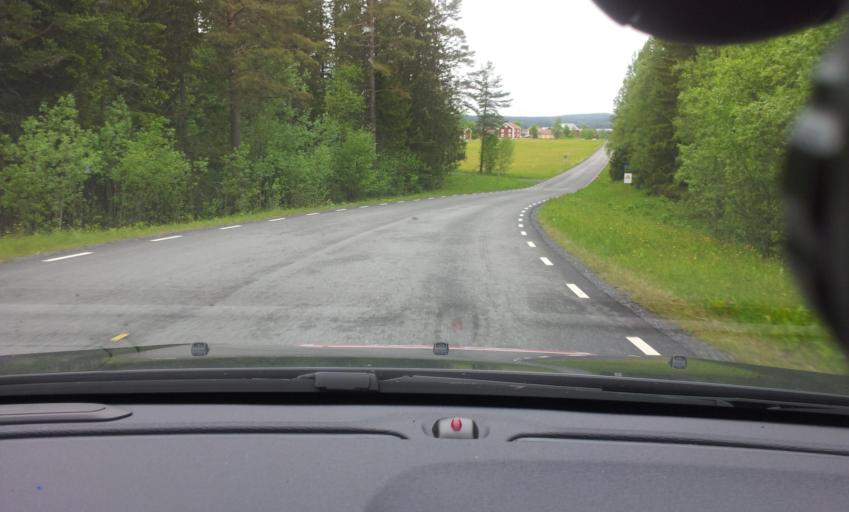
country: SE
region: Jaemtland
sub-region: Krokoms Kommun
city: Valla
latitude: 63.3249
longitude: 14.0486
